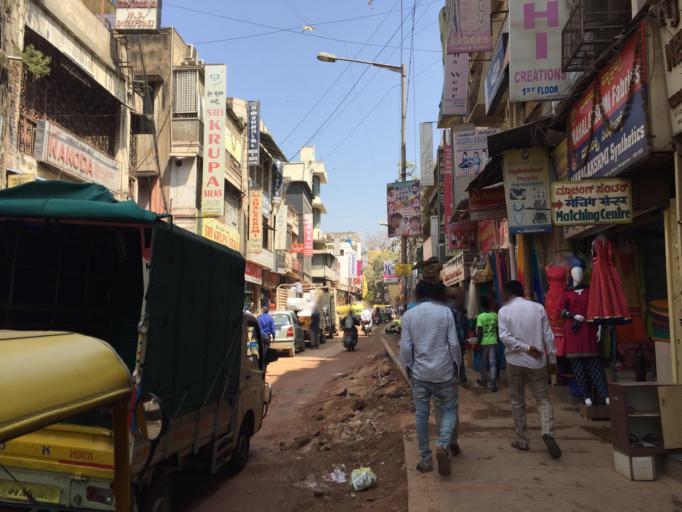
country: IN
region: Karnataka
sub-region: Bangalore Urban
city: Bangalore
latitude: 12.9689
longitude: 77.5793
